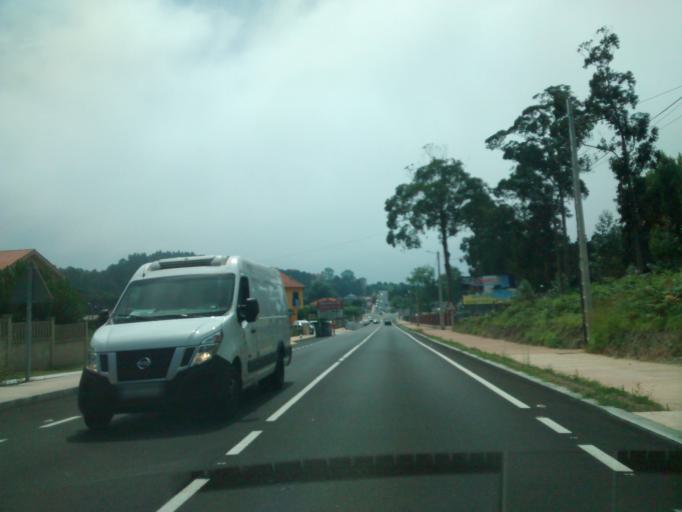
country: ES
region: Galicia
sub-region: Provincia de Pontevedra
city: Sanxenxo
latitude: 42.4190
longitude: -8.8706
